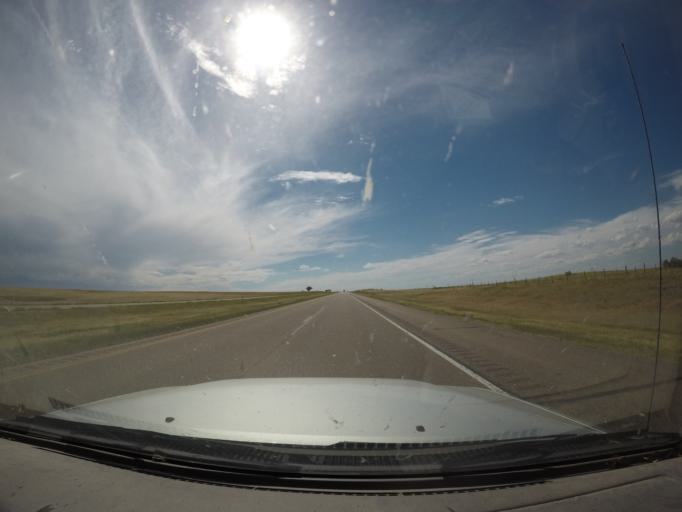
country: US
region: Colorado
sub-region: Sedgwick County
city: Julesburg
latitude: 41.0479
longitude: -102.3318
